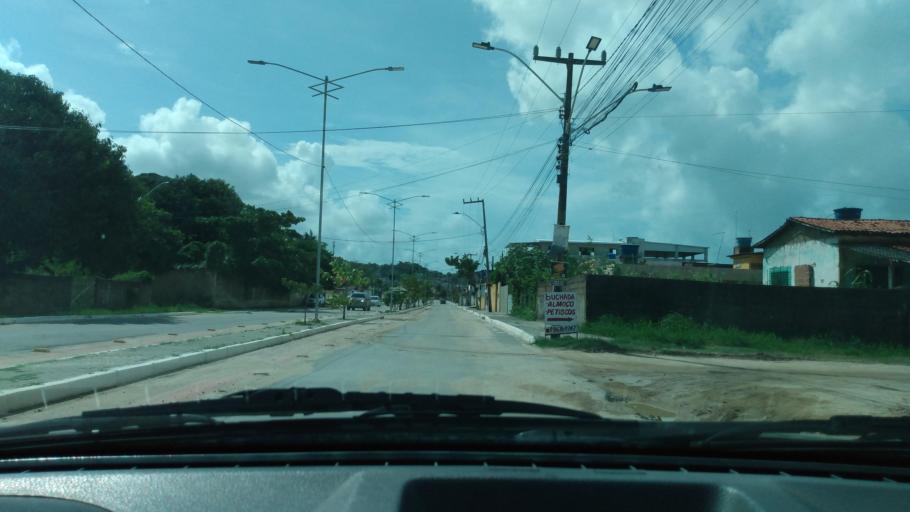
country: BR
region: Pernambuco
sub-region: Cabo De Santo Agostinho
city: Cabo
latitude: -8.3246
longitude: -34.9533
